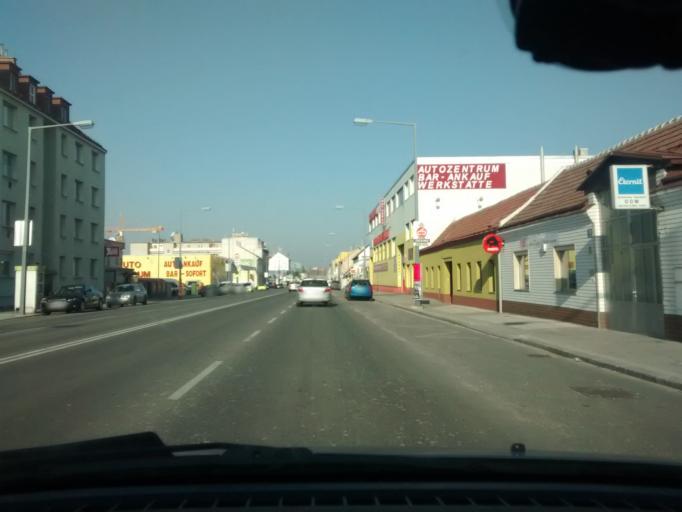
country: AT
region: Lower Austria
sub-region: Politischer Bezirk Modling
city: Vosendorf
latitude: 48.1441
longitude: 16.3313
